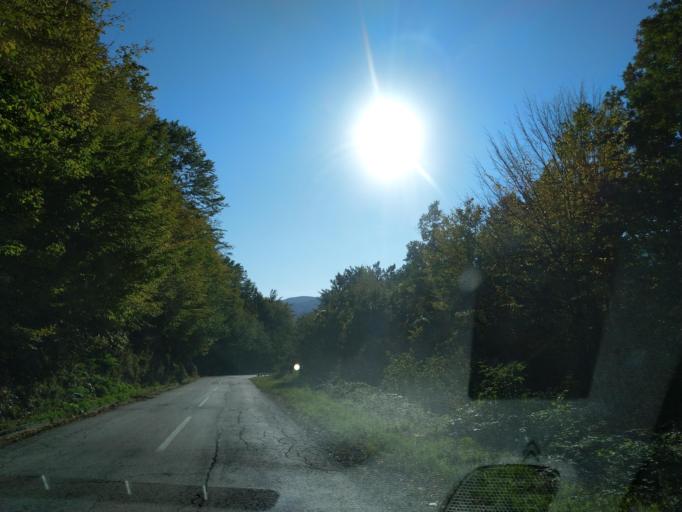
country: RS
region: Central Serbia
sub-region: Moravicki Okrug
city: Ivanjica
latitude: 43.4736
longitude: 20.2445
